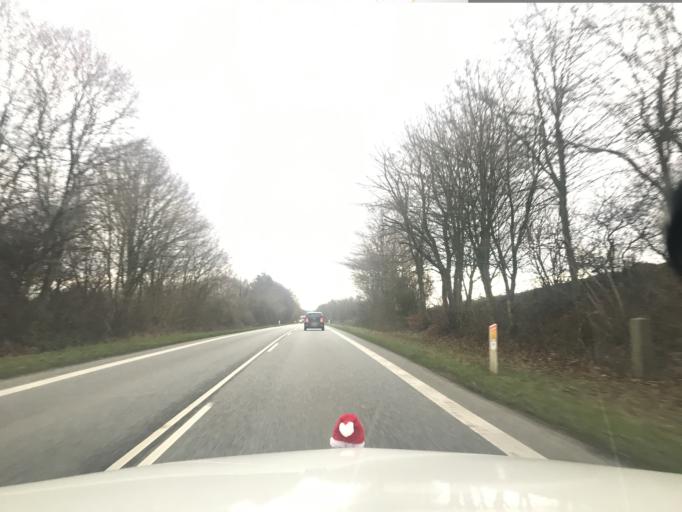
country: DE
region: Schleswig-Holstein
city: Glucksburg
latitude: 54.8890
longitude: 9.5167
